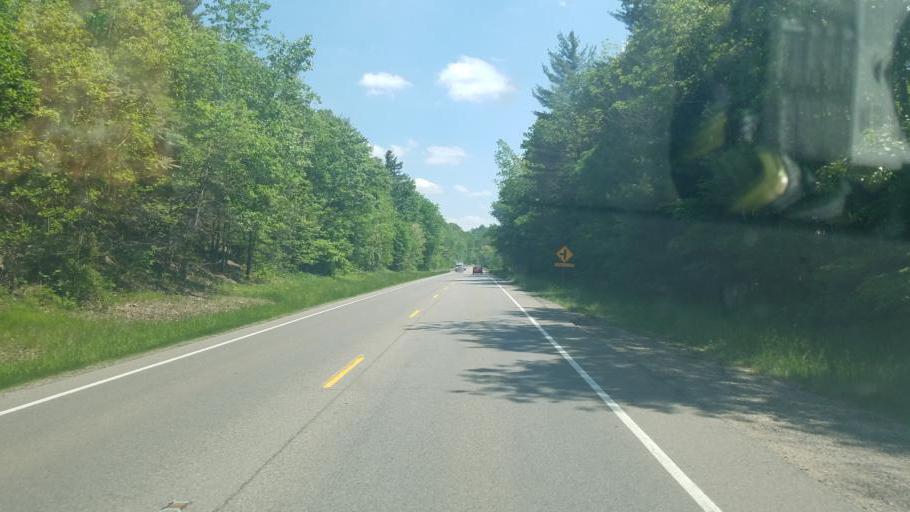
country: US
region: Ohio
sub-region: Muskingum County
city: North Zanesville
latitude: 40.0193
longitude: -82.0901
